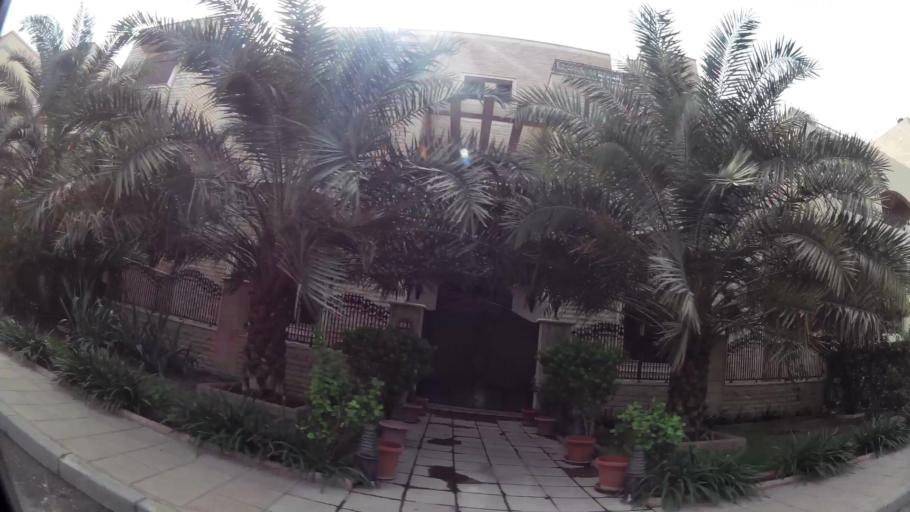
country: KW
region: Mubarak al Kabir
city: Sabah as Salim
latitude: 29.2711
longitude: 48.0318
